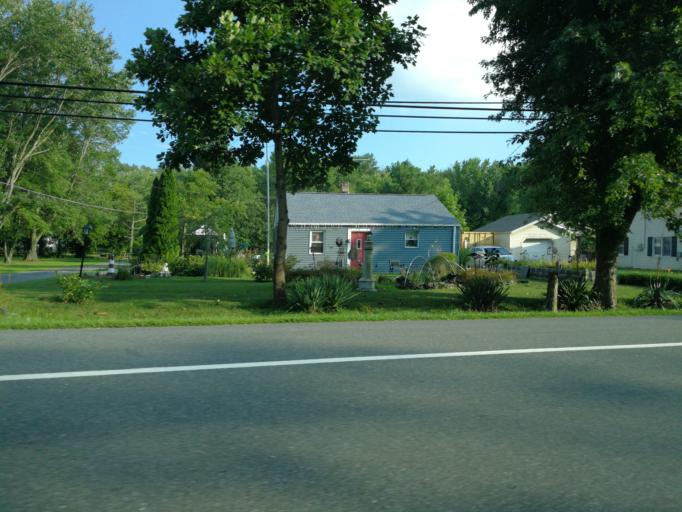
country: US
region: Maryland
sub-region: Harford County
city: Perryman
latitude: 39.4902
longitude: -76.2101
